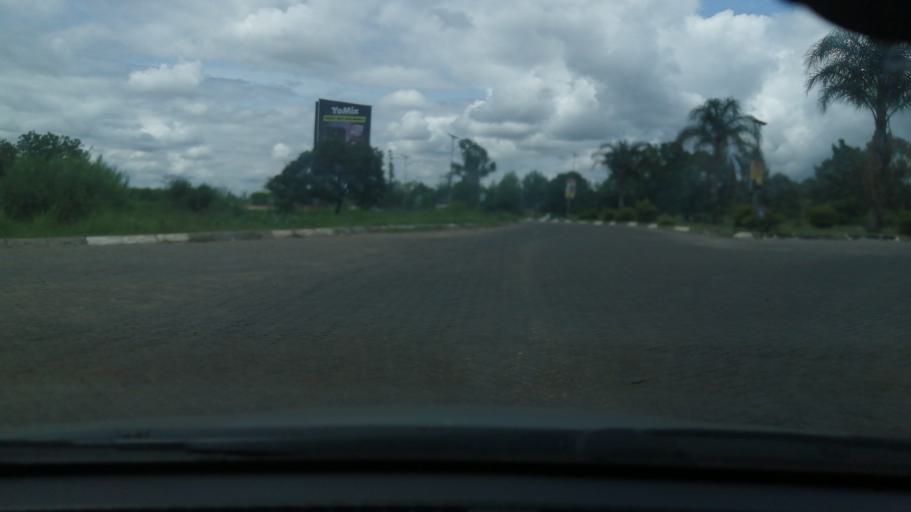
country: ZW
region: Harare
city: Harare
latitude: -17.8030
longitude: 31.0760
